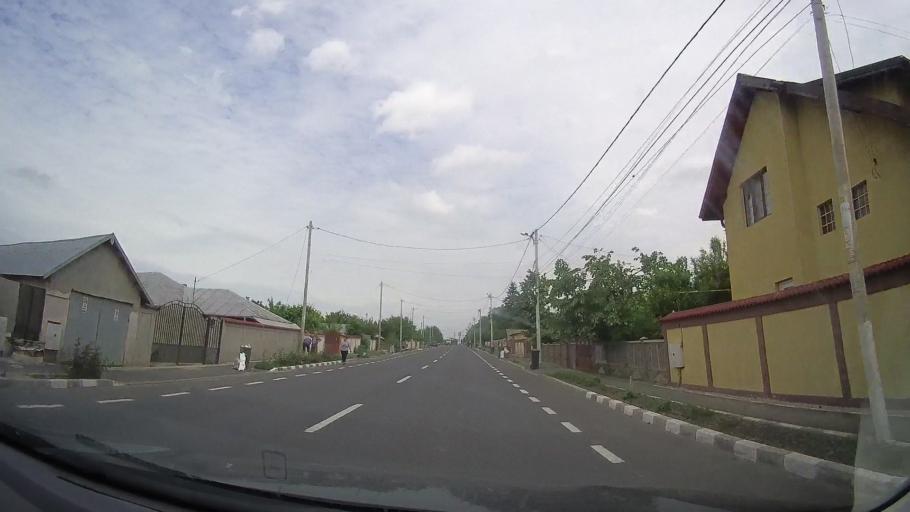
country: RO
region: Teleorman
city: Rosiori de Vede
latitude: 44.0964
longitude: 24.9927
